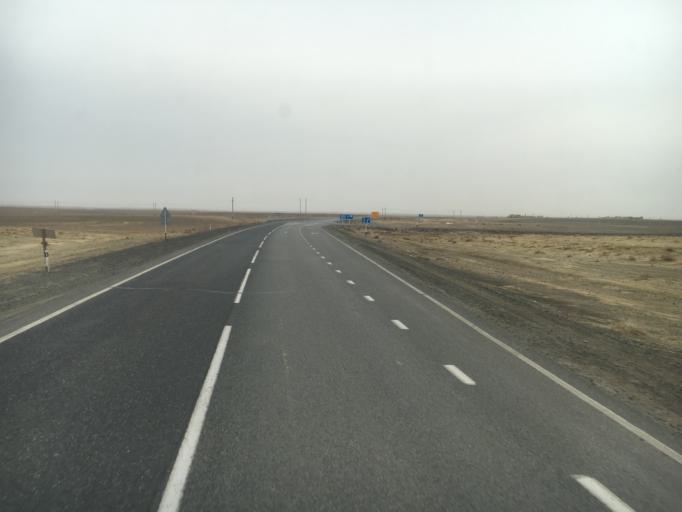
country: KZ
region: Qyzylorda
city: Aral
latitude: 46.8240
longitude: 61.7051
